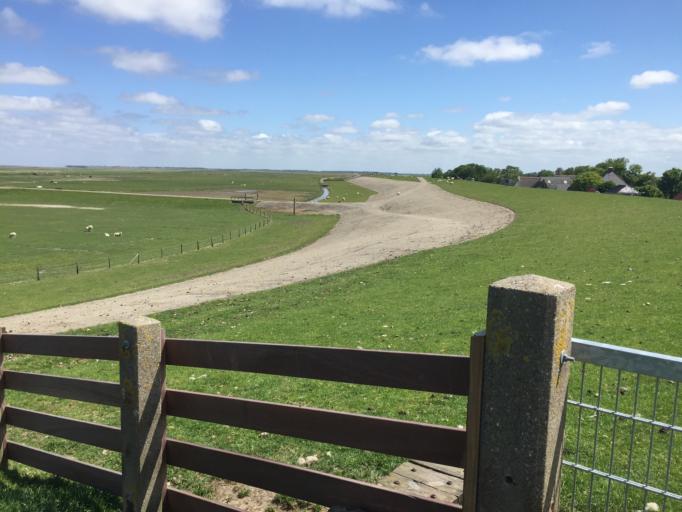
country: NL
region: Friesland
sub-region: Gemeente Dongeradeel
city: Anjum
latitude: 53.4031
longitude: 6.0842
